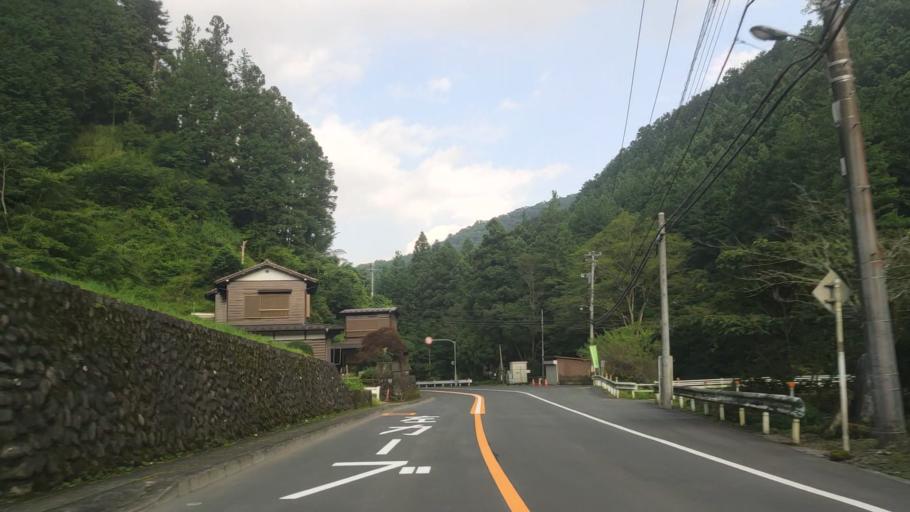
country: JP
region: Tokyo
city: Ome
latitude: 35.8318
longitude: 139.2266
